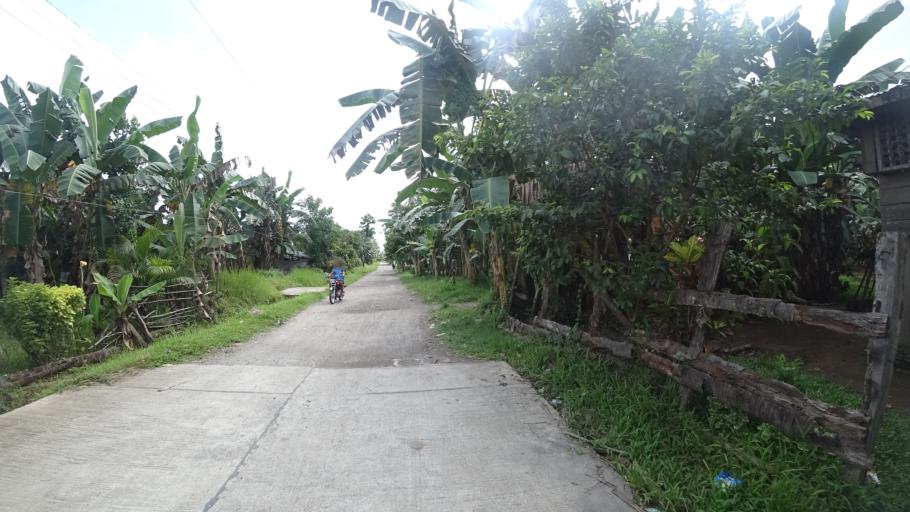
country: PH
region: Eastern Visayas
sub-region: Province of Leyte
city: Pastrana
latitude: 11.1629
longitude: 124.8665
